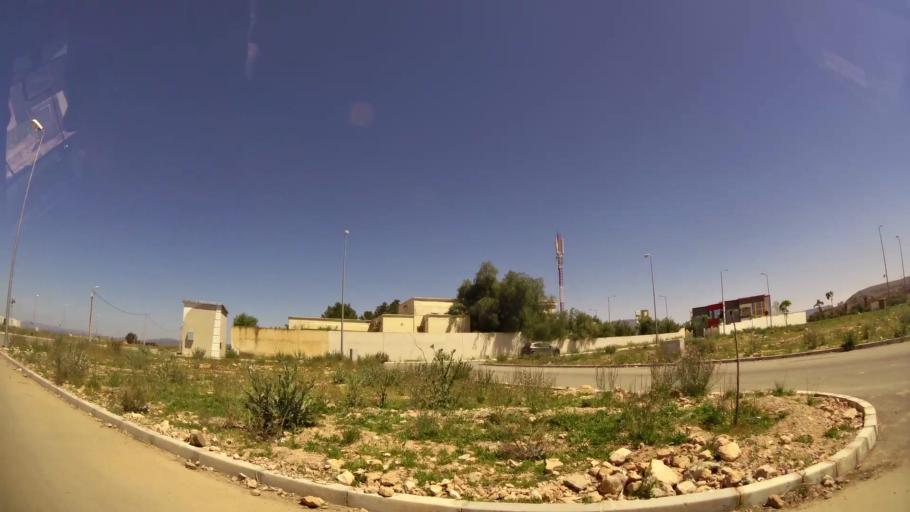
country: MA
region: Oriental
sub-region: Oujda-Angad
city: Oujda
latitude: 34.6674
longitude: -1.8683
